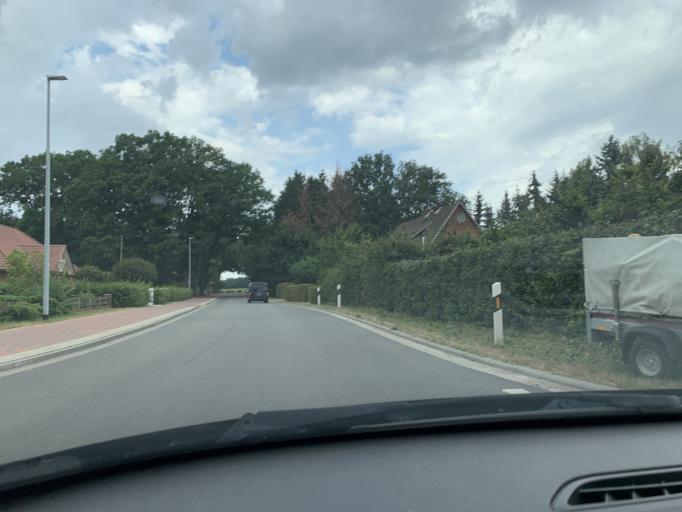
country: DE
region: Lower Saxony
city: Dohren
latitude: 53.2958
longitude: 9.6839
